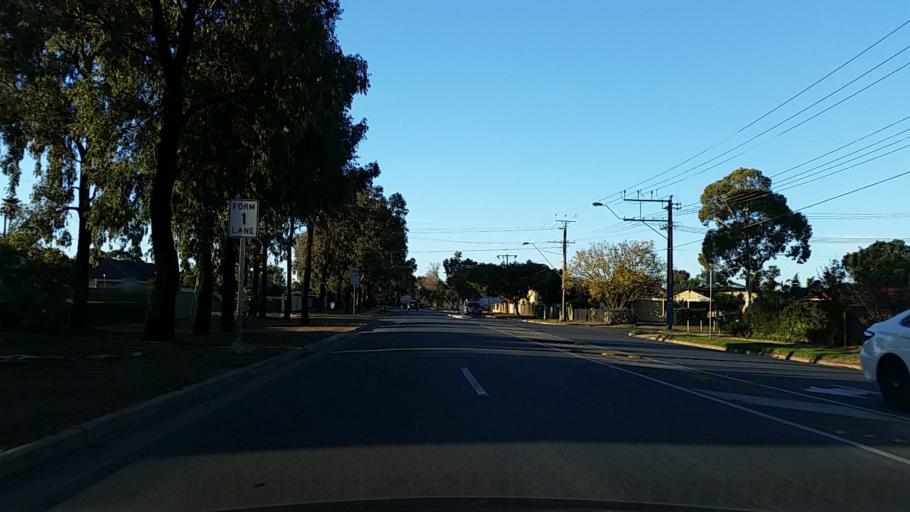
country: AU
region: South Australia
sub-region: Salisbury
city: Salisbury
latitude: -34.7683
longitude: 138.6519
